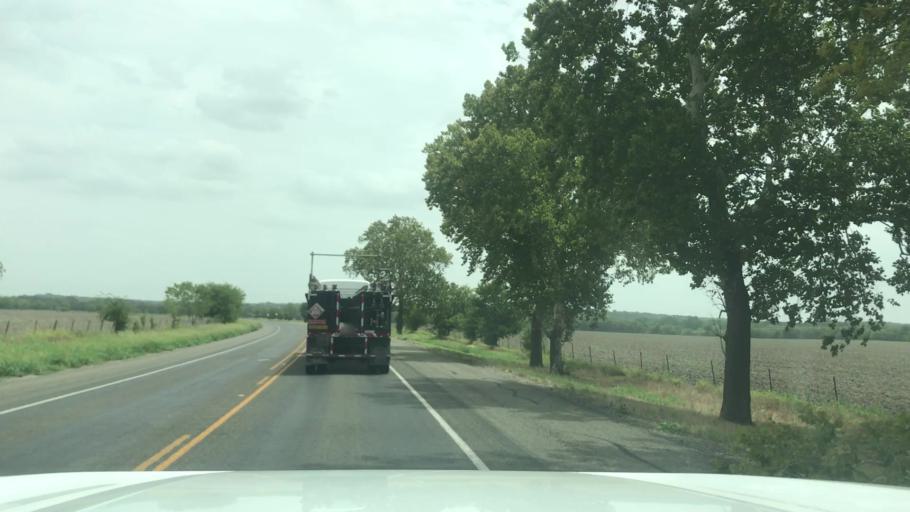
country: US
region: Texas
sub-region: Bosque County
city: Valley Mills
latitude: 31.6664
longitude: -97.4952
